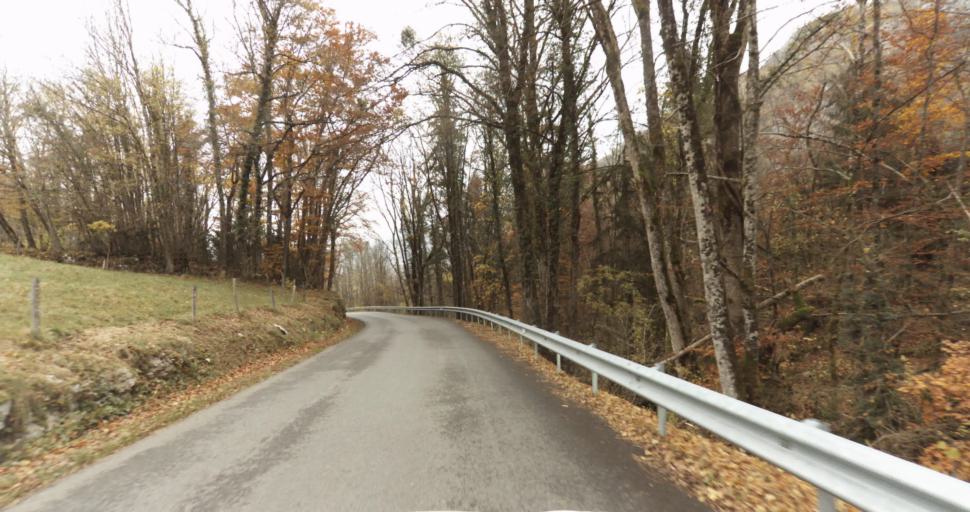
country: FR
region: Rhone-Alpes
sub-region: Departement de la Haute-Savoie
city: Talloires
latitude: 45.8142
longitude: 6.1956
